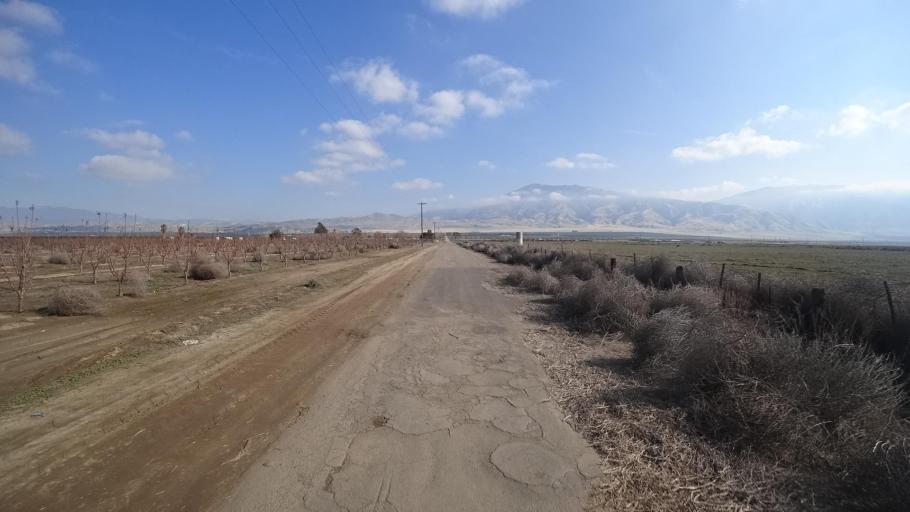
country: US
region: California
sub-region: Kern County
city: Arvin
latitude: 35.2385
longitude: -118.7818
